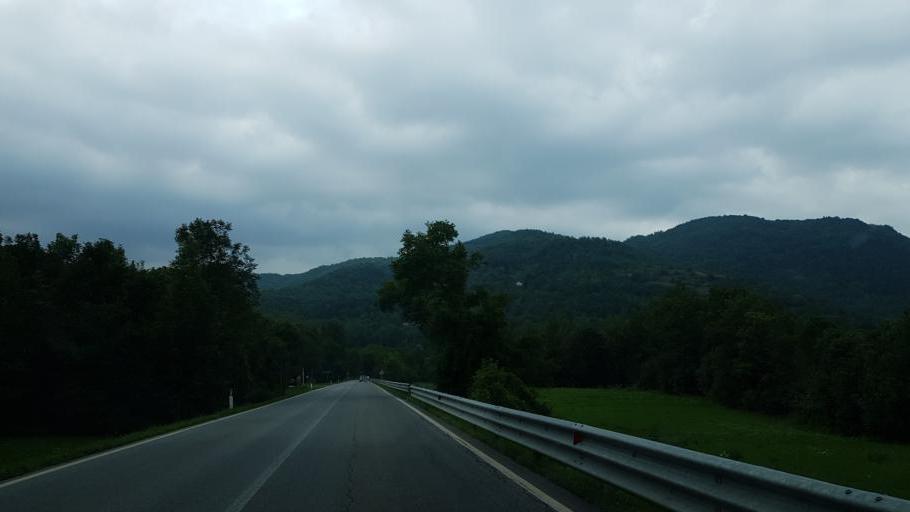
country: IT
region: Piedmont
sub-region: Provincia di Cuneo
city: Moiola
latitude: 44.3270
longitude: 7.3968
